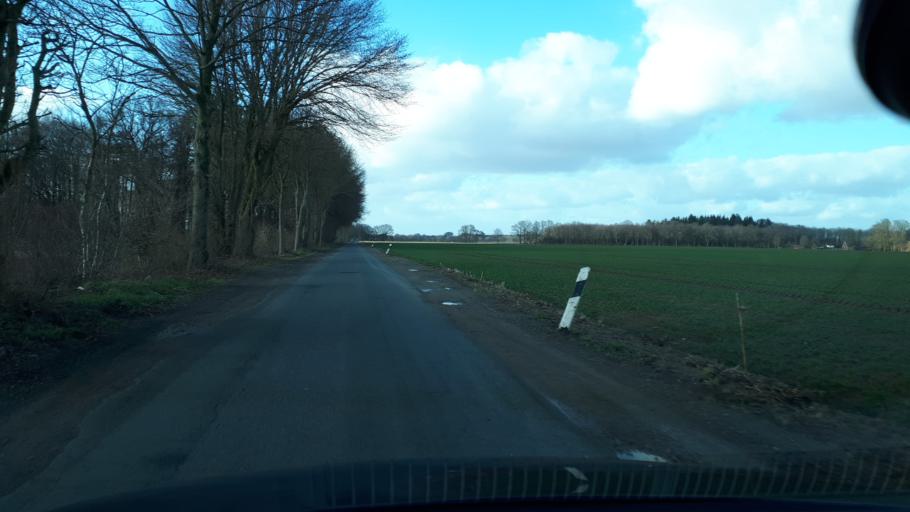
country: DE
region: Lower Saxony
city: Cloppenburg
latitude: 52.8367
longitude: 7.9979
